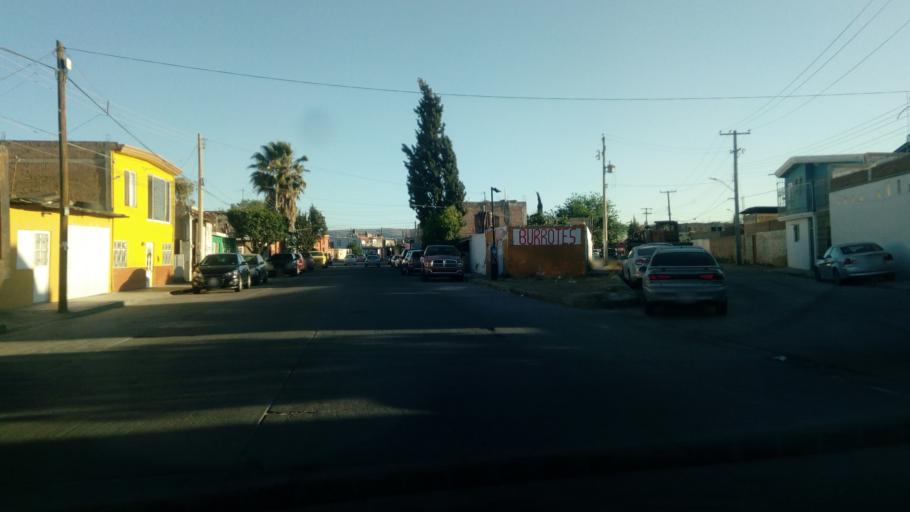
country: MX
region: Durango
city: Victoria de Durango
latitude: 24.0016
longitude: -104.6797
